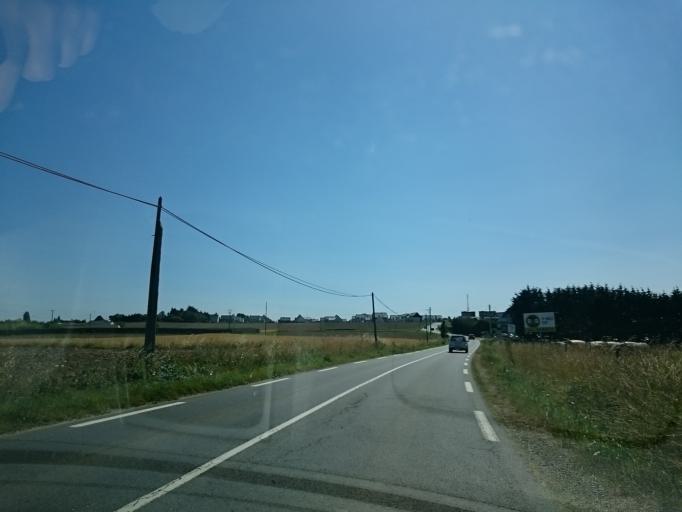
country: FR
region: Brittany
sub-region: Departement d'Ille-et-Vilaine
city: Saint-Coulomb
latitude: 48.6633
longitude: -1.9594
